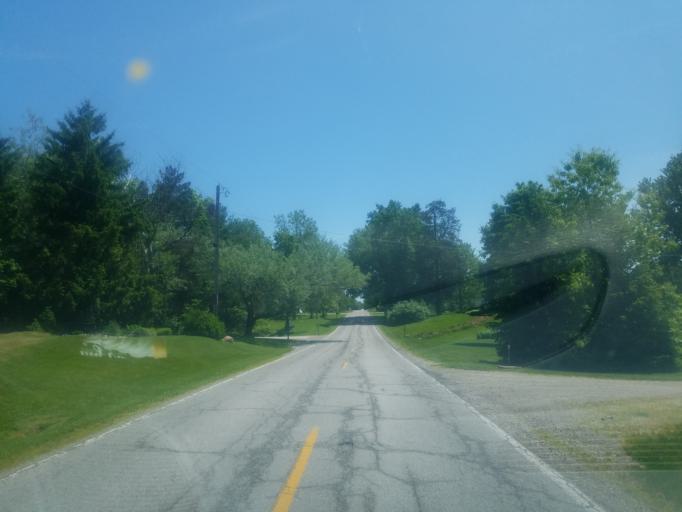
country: US
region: Ohio
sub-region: Huron County
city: Wakeman
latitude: 41.1967
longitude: -82.3730
